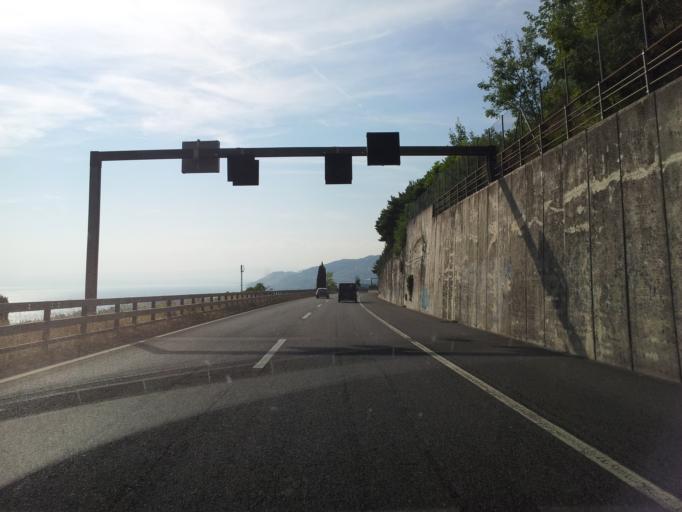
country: CH
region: Vaud
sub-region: Riviera-Pays-d'Enhaut District
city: Montreux
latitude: 46.4423
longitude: 6.9102
